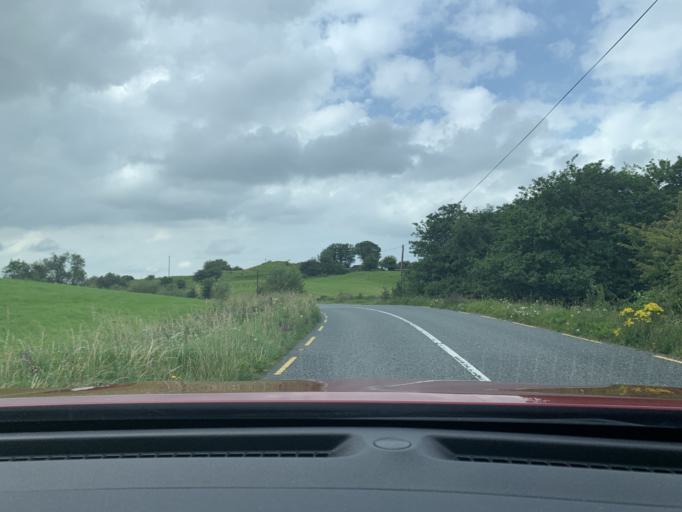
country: IE
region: Connaught
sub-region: Maigh Eo
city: Kiltamagh
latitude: 53.8570
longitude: -8.9106
